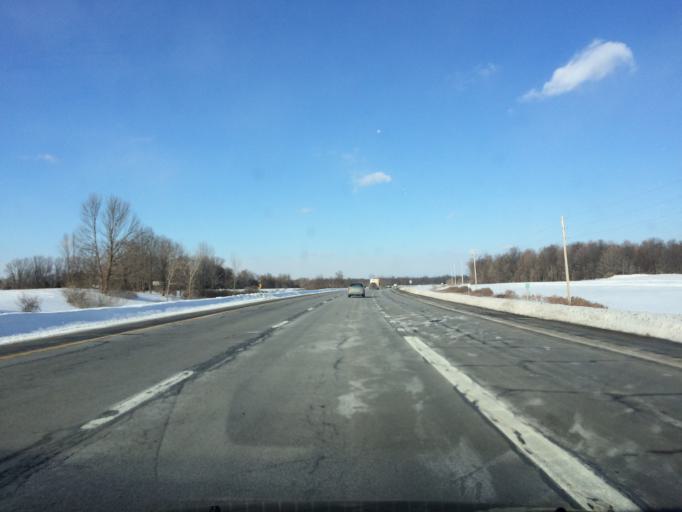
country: US
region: New York
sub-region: Genesee County
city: Bergen
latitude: 43.0776
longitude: -77.9319
